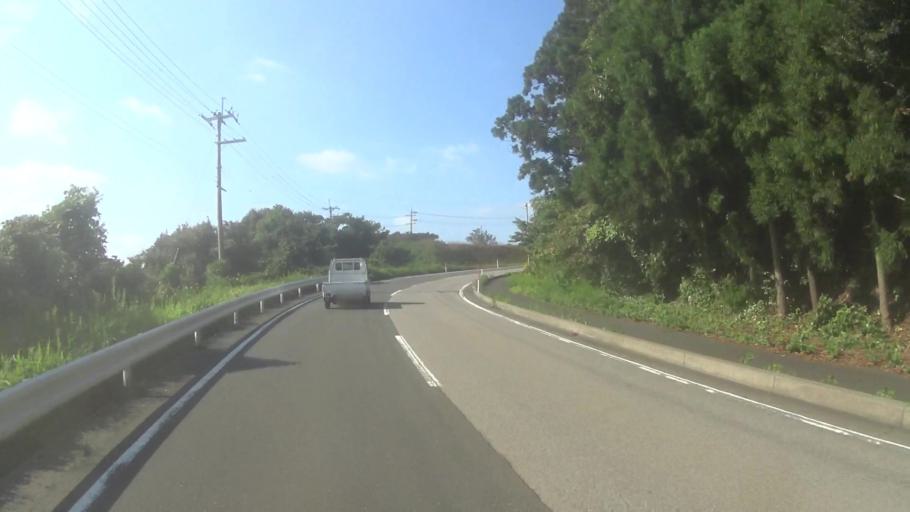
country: JP
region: Kyoto
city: Miyazu
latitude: 35.6925
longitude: 135.0503
